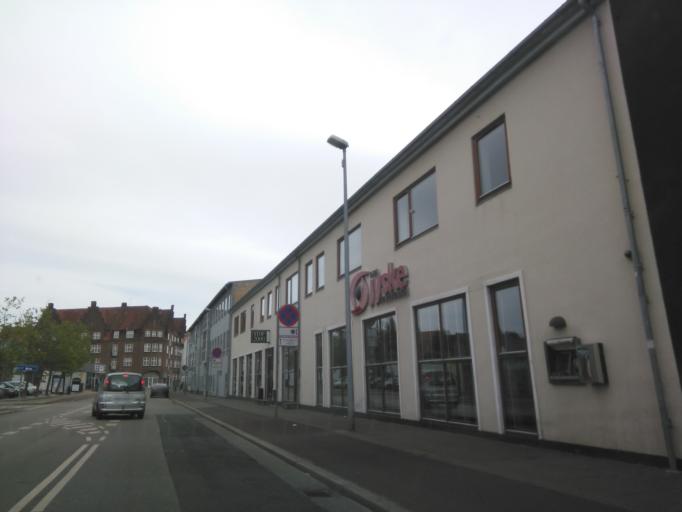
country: DK
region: Central Jutland
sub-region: Horsens Kommune
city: Horsens
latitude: 55.8603
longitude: 9.8432
